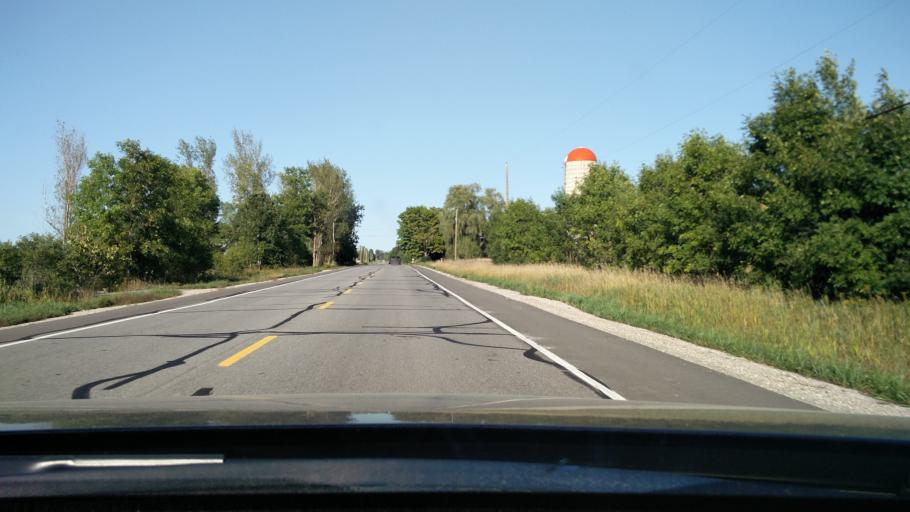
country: CA
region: Ontario
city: Perth
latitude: 44.9527
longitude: -76.1661
